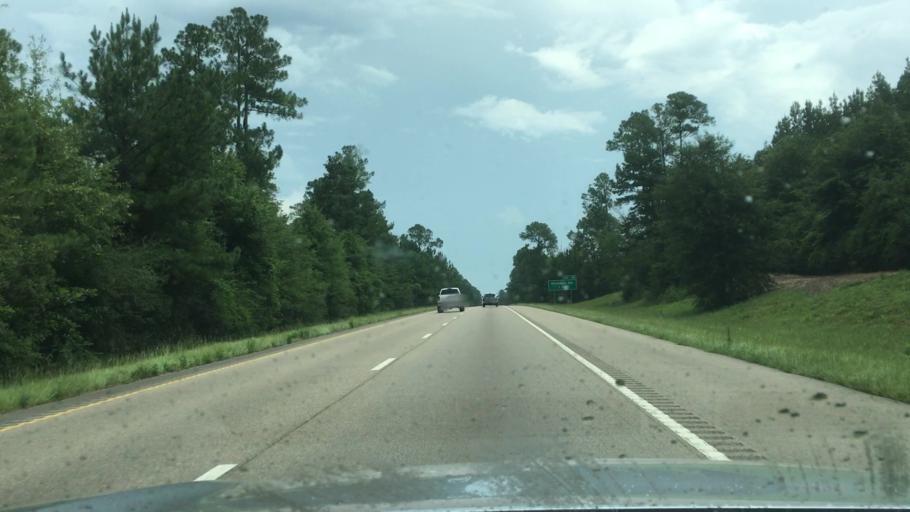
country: US
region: Mississippi
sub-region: Pearl River County
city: Poplarville
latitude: 30.9074
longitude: -89.4682
